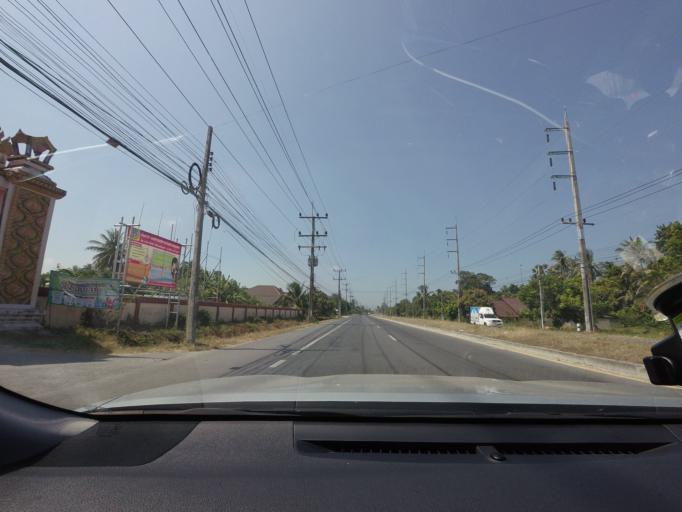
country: TH
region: Songkhla
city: Krasae Sin
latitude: 7.6189
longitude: 100.3963
